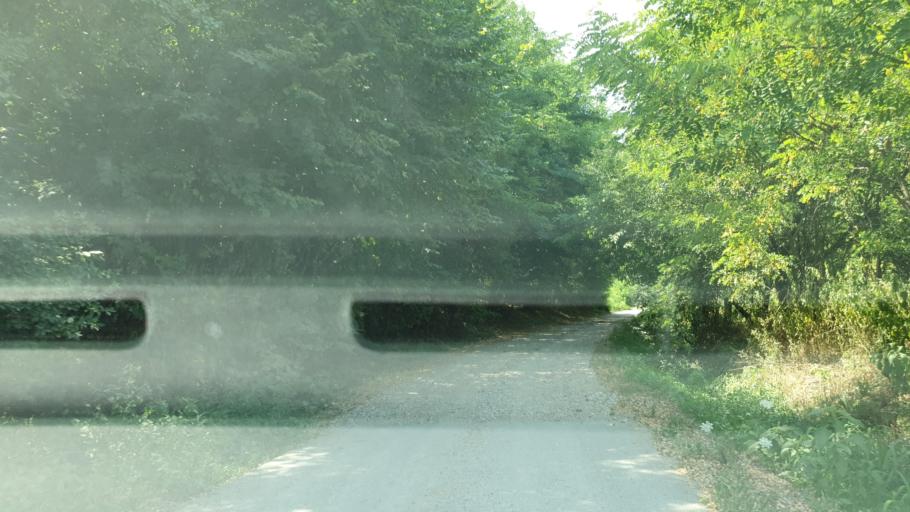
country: BA
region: Republika Srpska
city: Bijeljina
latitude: 44.7216
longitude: 19.1931
